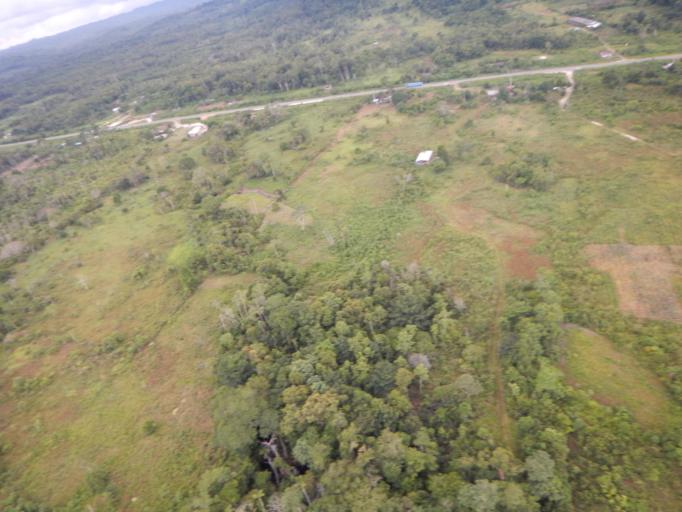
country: BO
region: Cochabamba
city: Chimore
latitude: -17.0004
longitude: -65.0550
